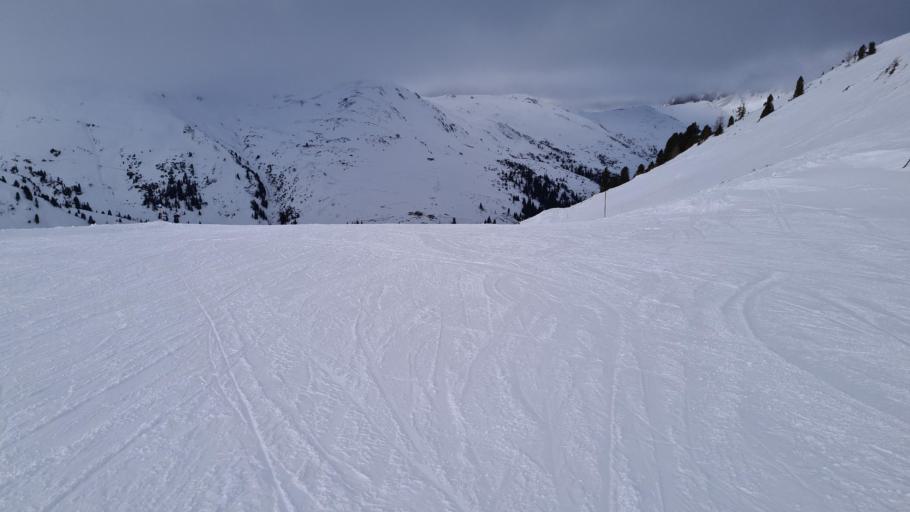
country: AT
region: Salzburg
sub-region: Politischer Bezirk Zell am See
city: Neukirchen am Grossvenediger
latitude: 47.2924
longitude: 12.2932
